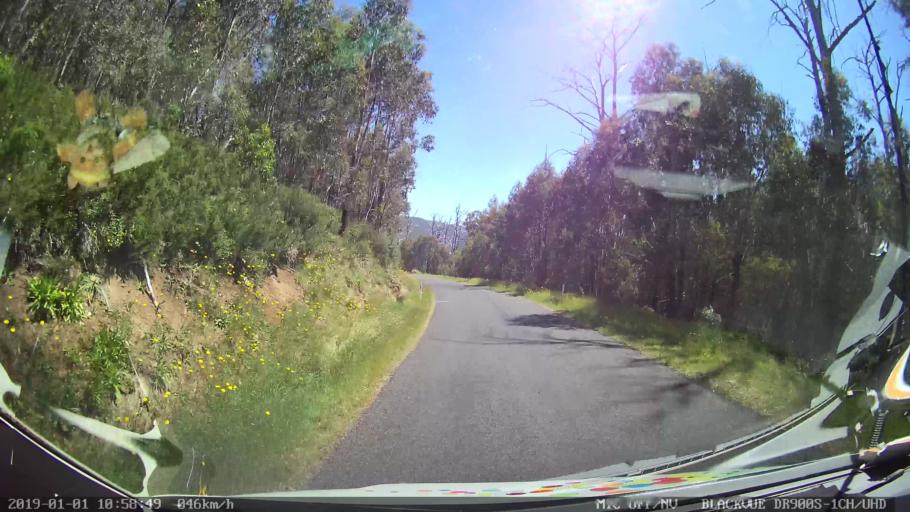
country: AU
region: New South Wales
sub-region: Snowy River
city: Jindabyne
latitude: -35.9898
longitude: 148.3984
